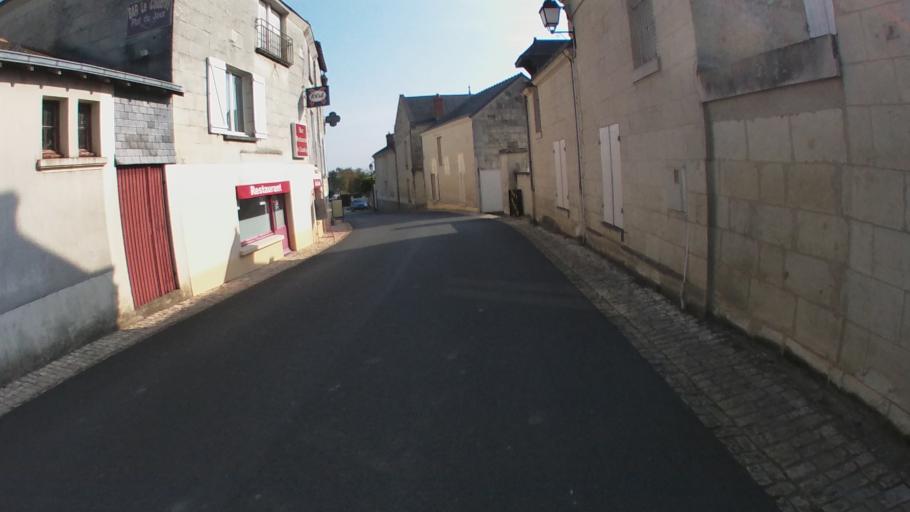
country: FR
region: Pays de la Loire
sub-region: Departement de Maine-et-Loire
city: Distre
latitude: 47.1932
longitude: -0.1186
